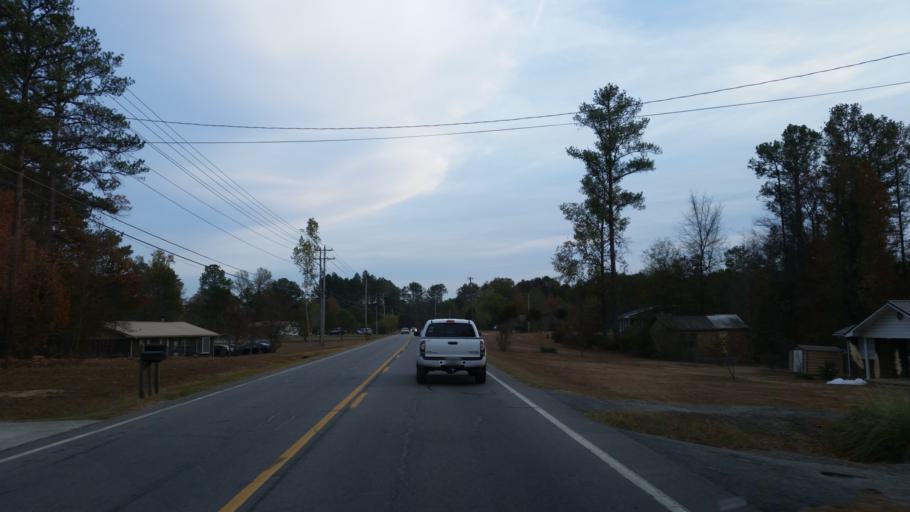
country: US
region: Georgia
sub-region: Gordon County
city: Calhoun
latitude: 34.5977
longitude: -84.9112
